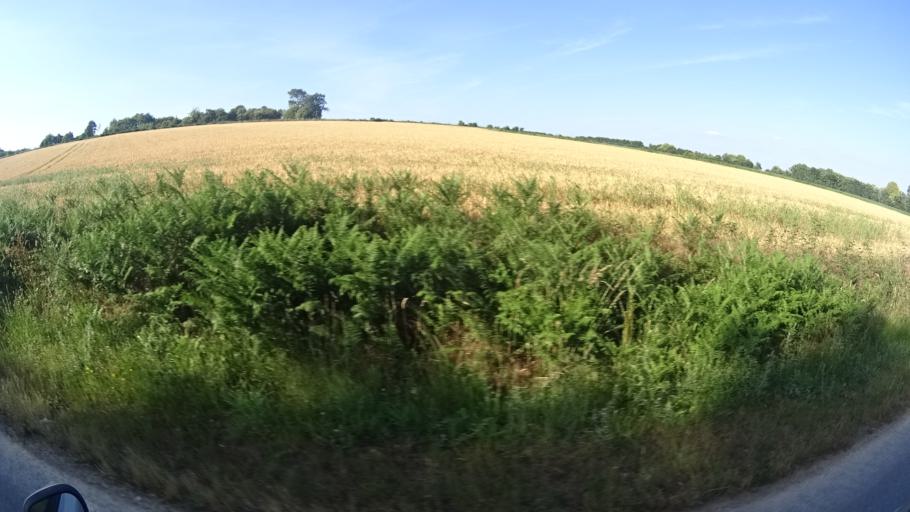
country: FR
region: Brittany
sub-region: Departement du Morbihan
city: Saint-Jean-la-Poterie
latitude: 47.6113
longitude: -2.1421
